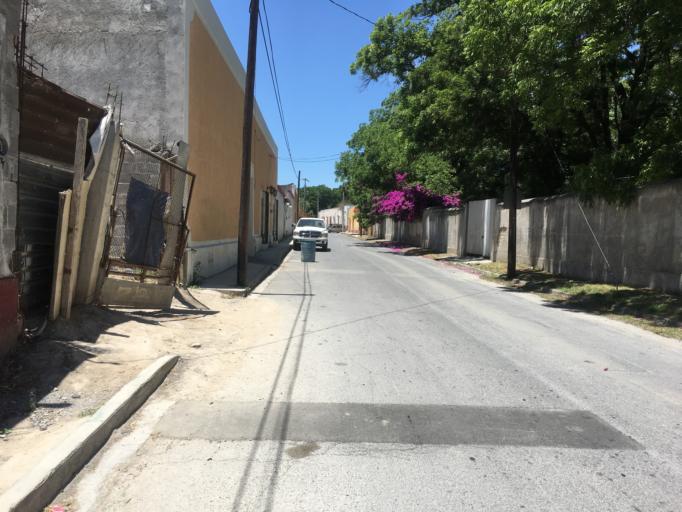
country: MX
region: Nuevo Leon
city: Garcia
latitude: 25.8106
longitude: -100.6068
